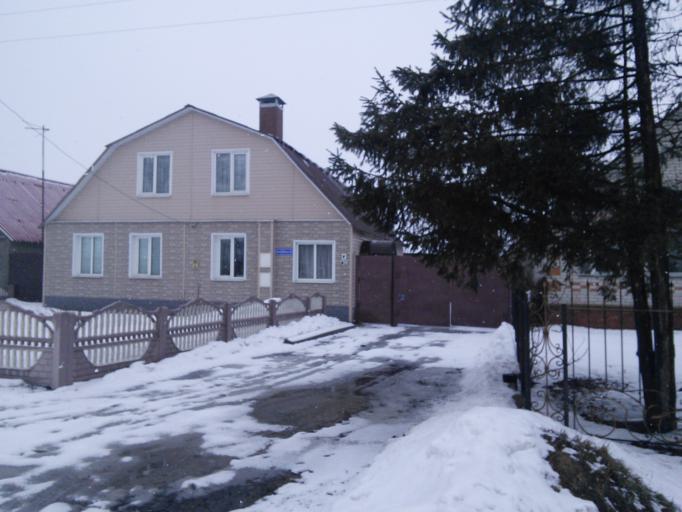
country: RU
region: Kursk
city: Chernitsyno
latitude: 51.5791
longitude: 36.0805
